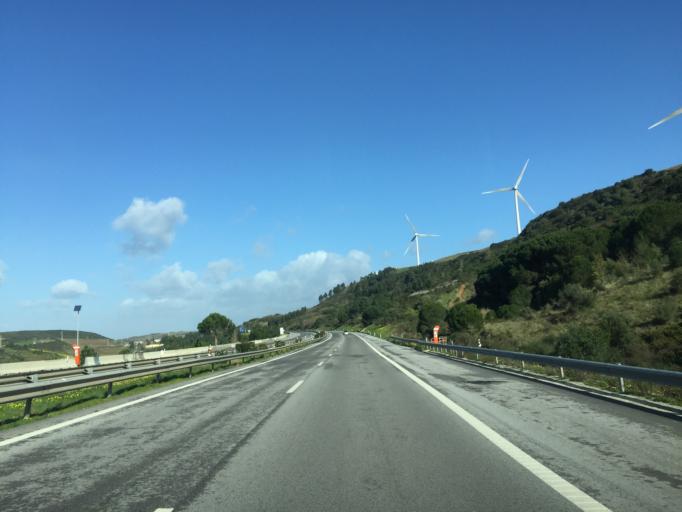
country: PT
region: Lisbon
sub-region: Torres Vedras
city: Torres Vedras
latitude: 39.0457
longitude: -9.2377
